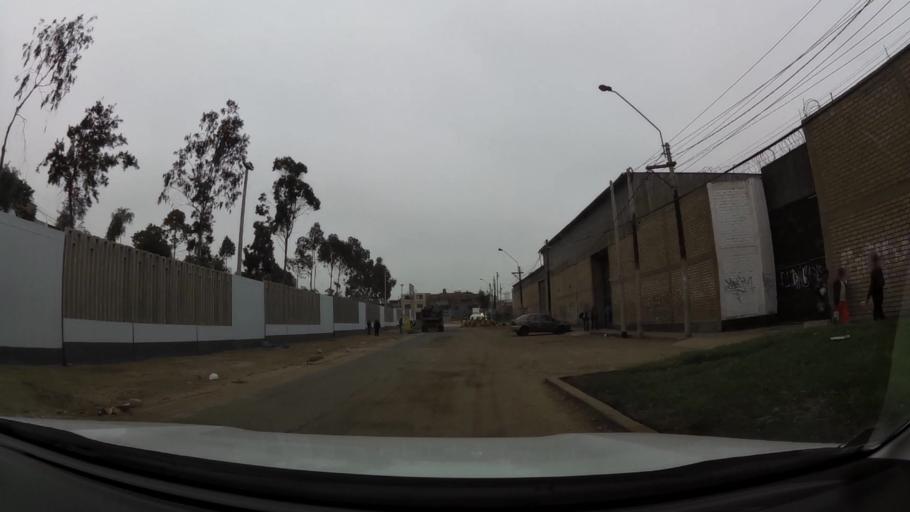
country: PE
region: Lima
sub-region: Lima
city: Surco
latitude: -12.1597
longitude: -76.9777
